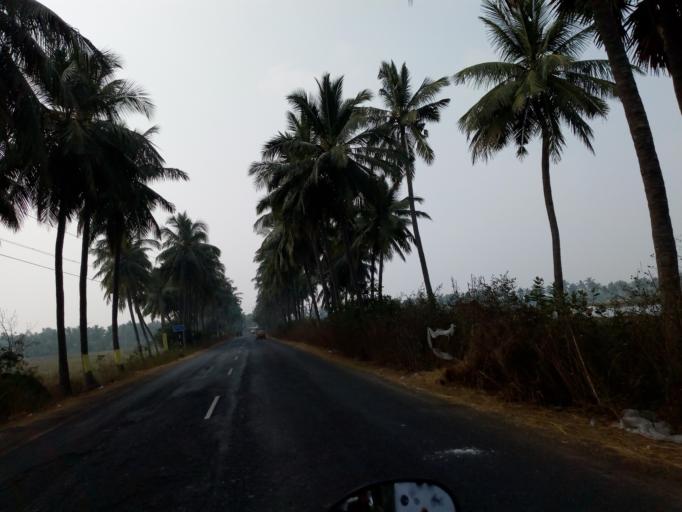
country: IN
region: Andhra Pradesh
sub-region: West Godavari
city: Akividu
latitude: 16.6243
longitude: 81.4623
